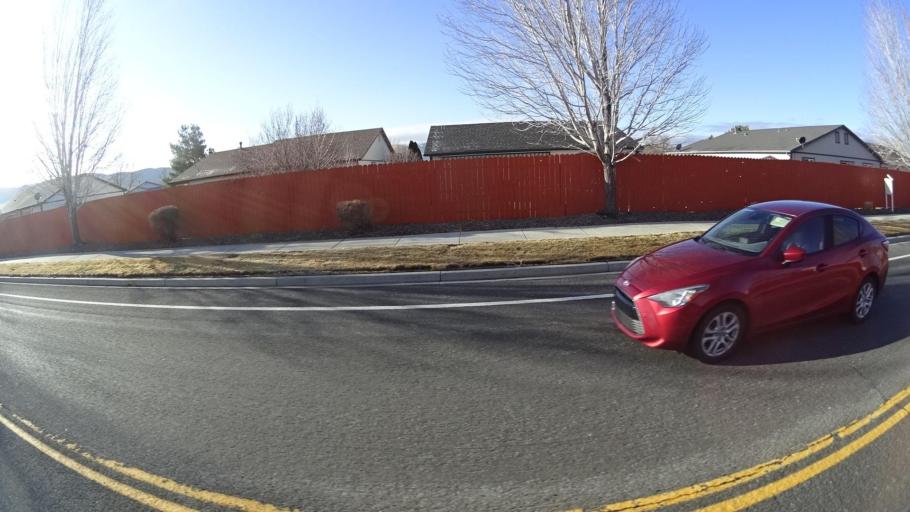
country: US
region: Nevada
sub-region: Washoe County
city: Cold Springs
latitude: 39.6876
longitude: -119.9712
